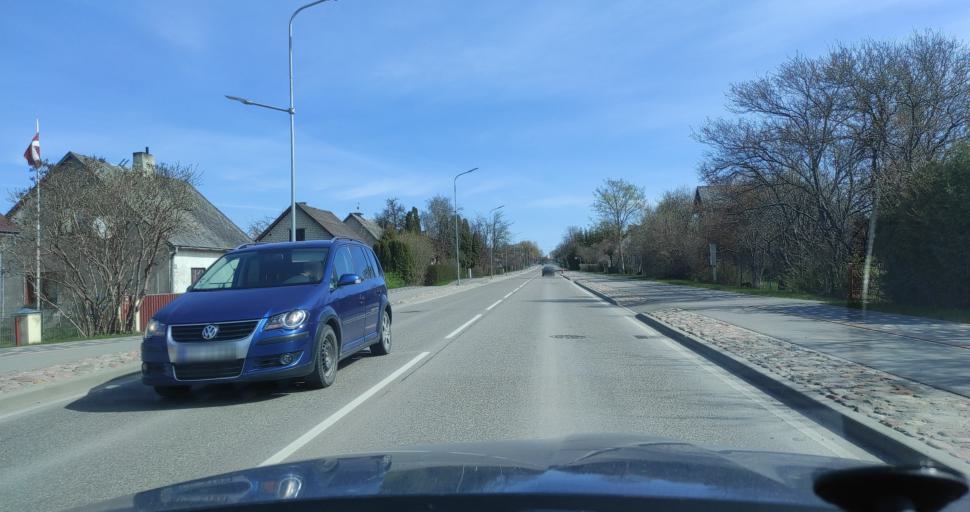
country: LV
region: Talsu Rajons
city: Talsi
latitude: 57.2384
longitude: 22.5734
